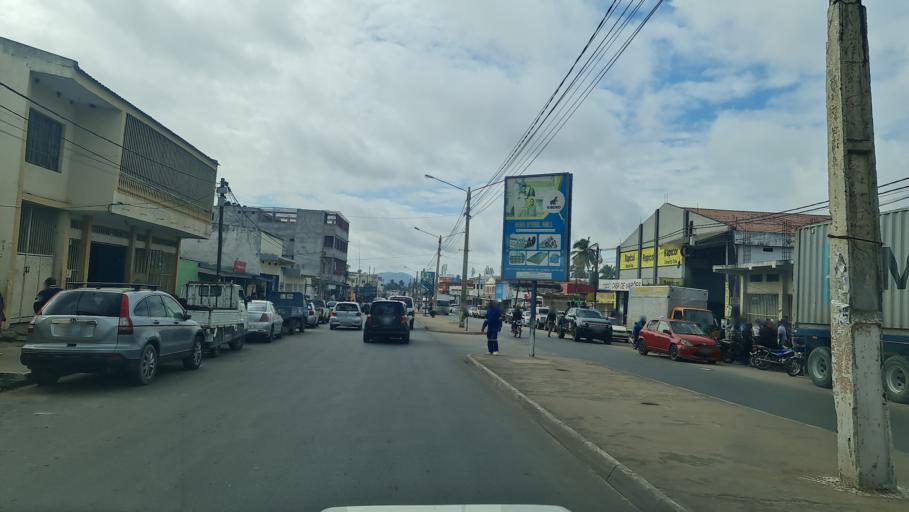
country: MZ
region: Nampula
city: Nampula
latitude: -15.1145
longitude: 39.2749
